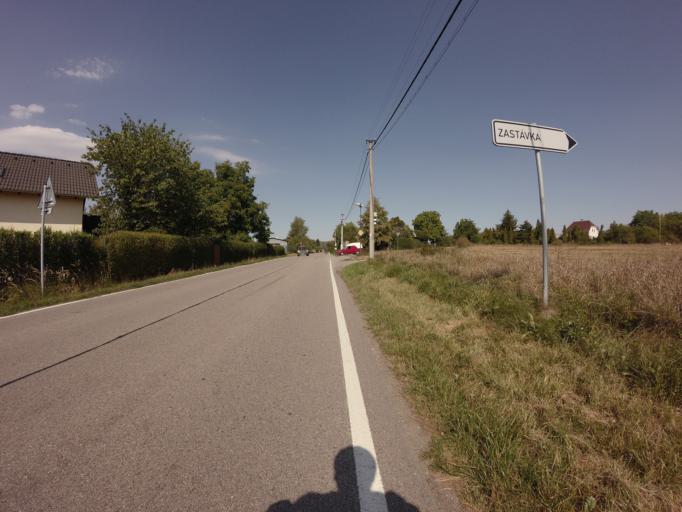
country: CZ
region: Central Bohemia
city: Kamenny Privoz
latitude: 49.8595
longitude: 14.5154
